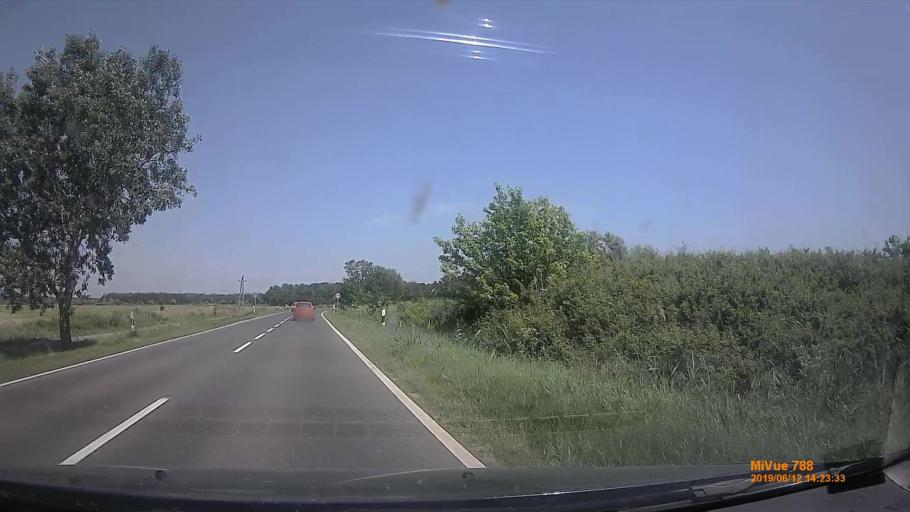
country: HU
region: Csongrad
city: Deszk
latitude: 46.2194
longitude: 20.2948
